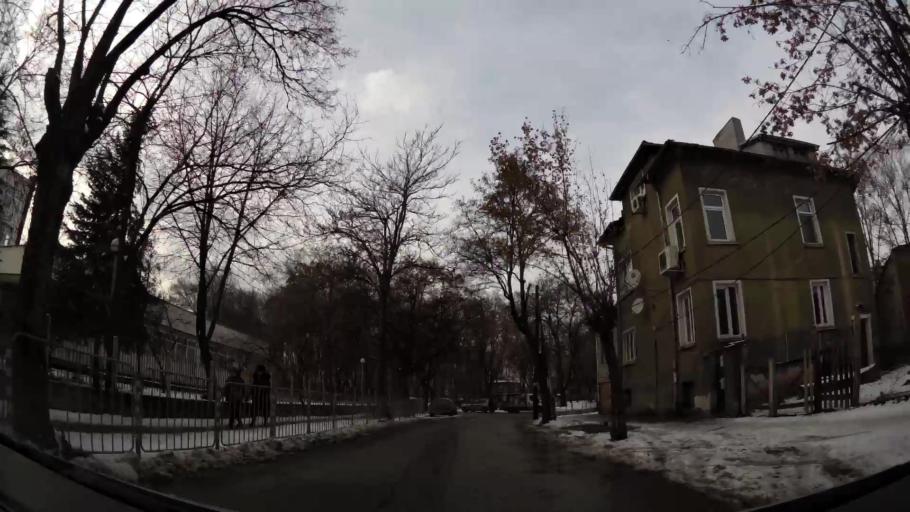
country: BG
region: Sofia-Capital
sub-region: Stolichna Obshtina
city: Sofia
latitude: 42.7067
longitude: 23.3457
